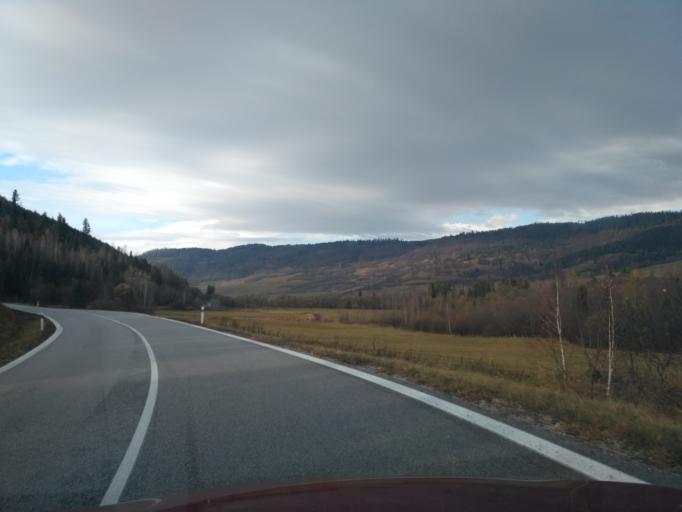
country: SK
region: Kosicky
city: Spisska Nova Ves
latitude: 48.8204
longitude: 20.6598
